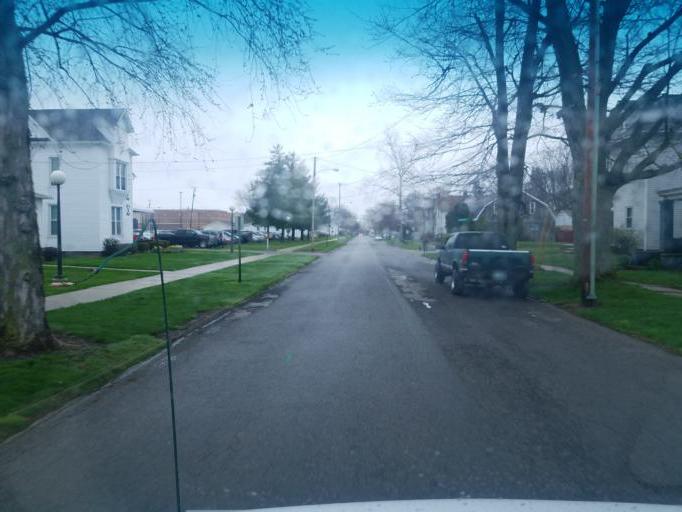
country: US
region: Ohio
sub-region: Hancock County
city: Findlay
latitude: 41.0515
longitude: -83.6542
